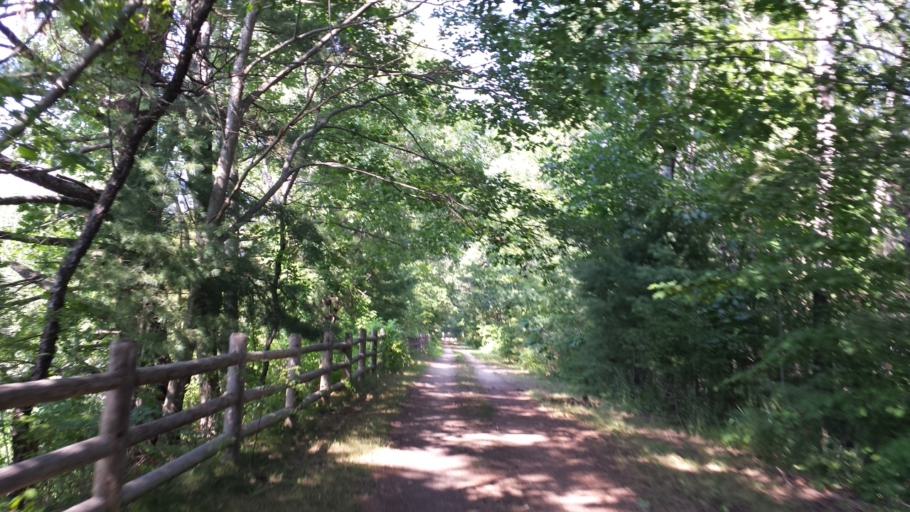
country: US
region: Maine
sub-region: York County
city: Biddeford
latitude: 43.4570
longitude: -70.5072
